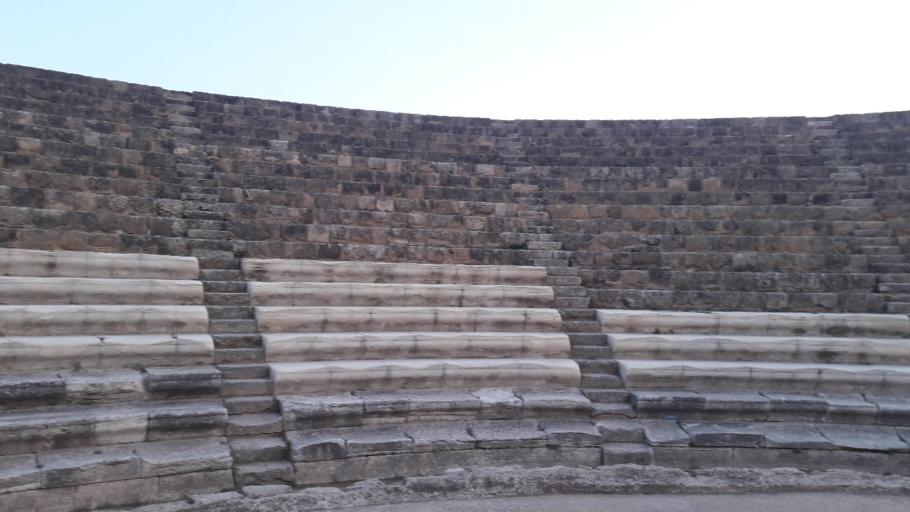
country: CY
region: Ammochostos
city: Famagusta
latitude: 35.1848
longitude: 33.9026
